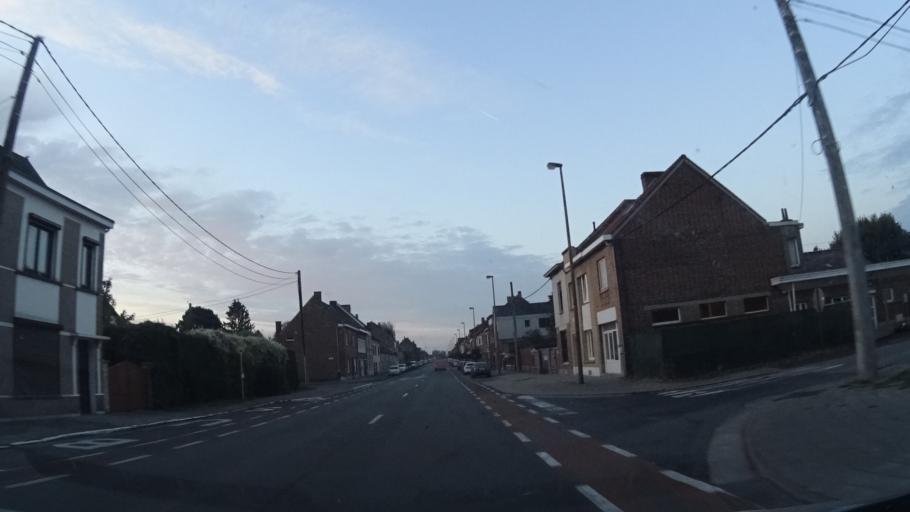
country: BE
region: Wallonia
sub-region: Province du Hainaut
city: Frasnes-lez-Buissenal
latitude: 50.5925
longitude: 3.6175
